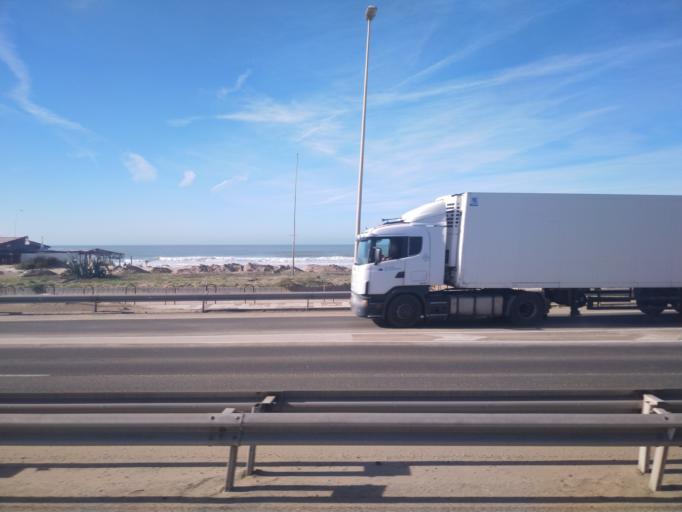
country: ES
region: Andalusia
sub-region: Provincia de Cadiz
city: Cadiz
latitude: 36.4892
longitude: -6.2671
